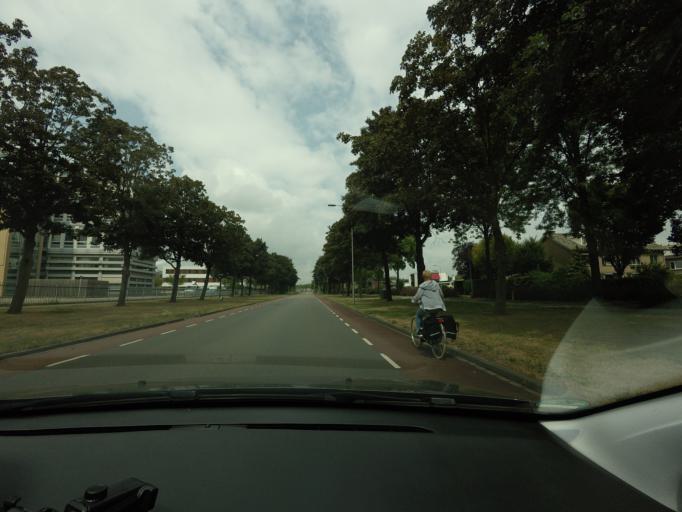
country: NL
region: Gelderland
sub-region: Gemeente Tiel
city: Tiel
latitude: 51.8809
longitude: 5.4207
